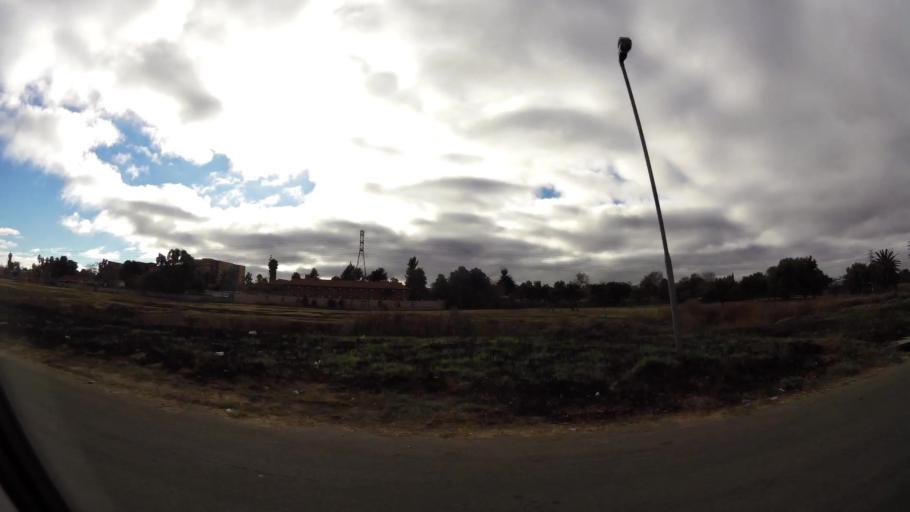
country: ZA
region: Limpopo
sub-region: Capricorn District Municipality
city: Polokwane
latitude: -23.9169
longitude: 29.4473
